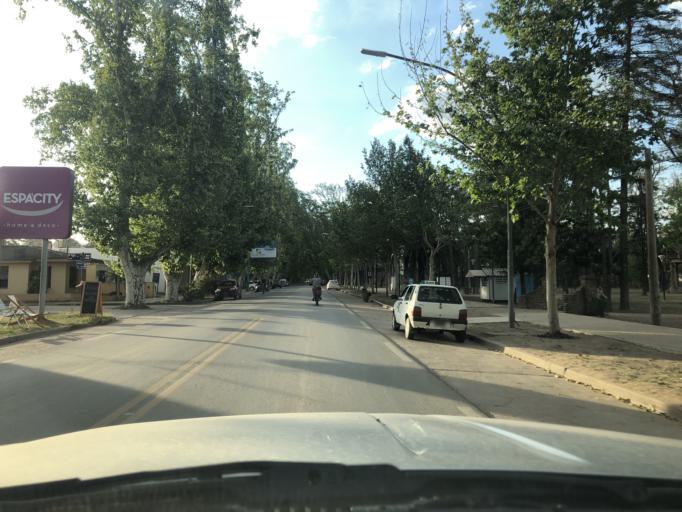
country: AR
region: Cordoba
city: Jesus Maria
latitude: -30.9986
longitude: -64.0883
